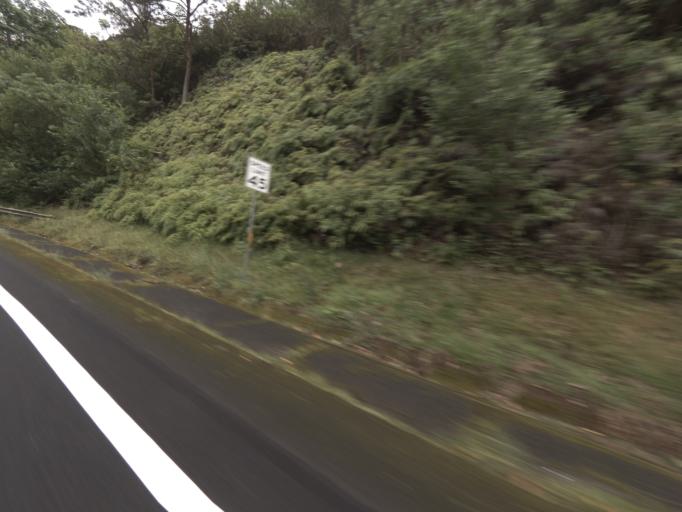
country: US
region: Hawaii
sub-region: Honolulu County
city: Kane'ohe
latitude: 21.3829
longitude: -157.8146
